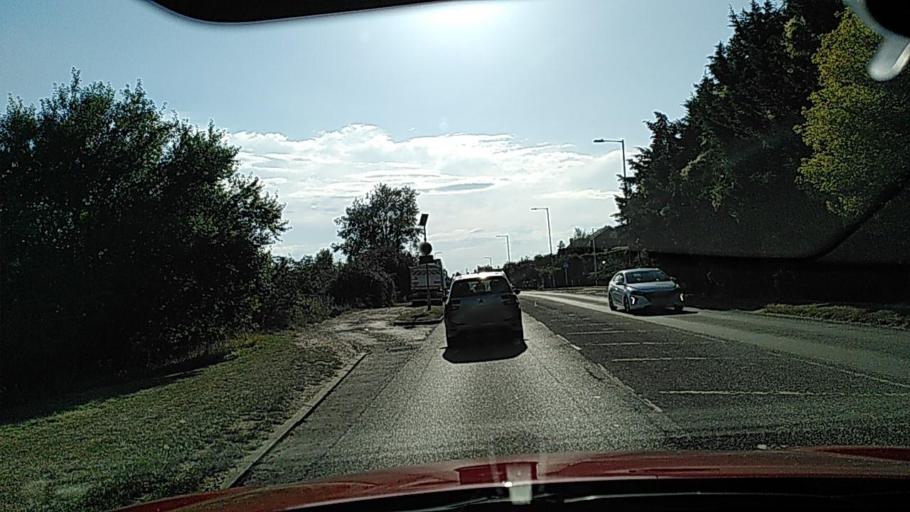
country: GB
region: England
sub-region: Wokingham
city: Sonning
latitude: 51.4744
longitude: -0.9436
